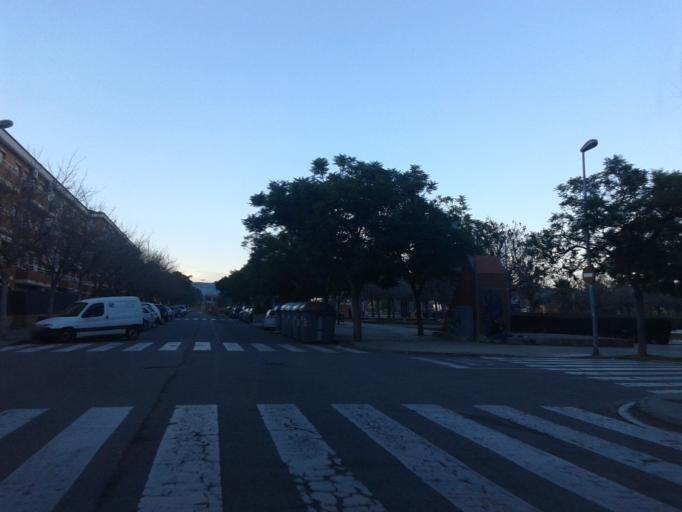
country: ES
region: Catalonia
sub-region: Provincia de Barcelona
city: Vilanova i la Geltru
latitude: 41.2227
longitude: 1.7102
